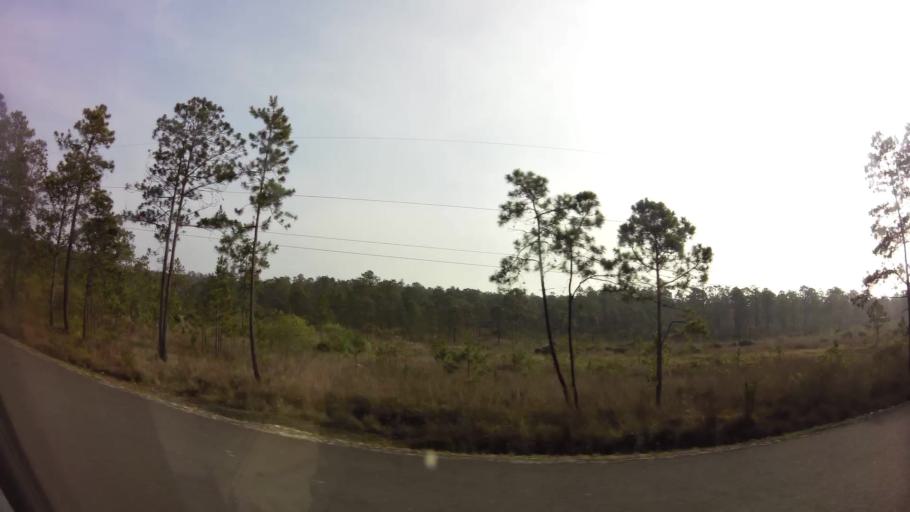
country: HN
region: Francisco Morazan
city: Zambrano
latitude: 14.2924
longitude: -87.4300
